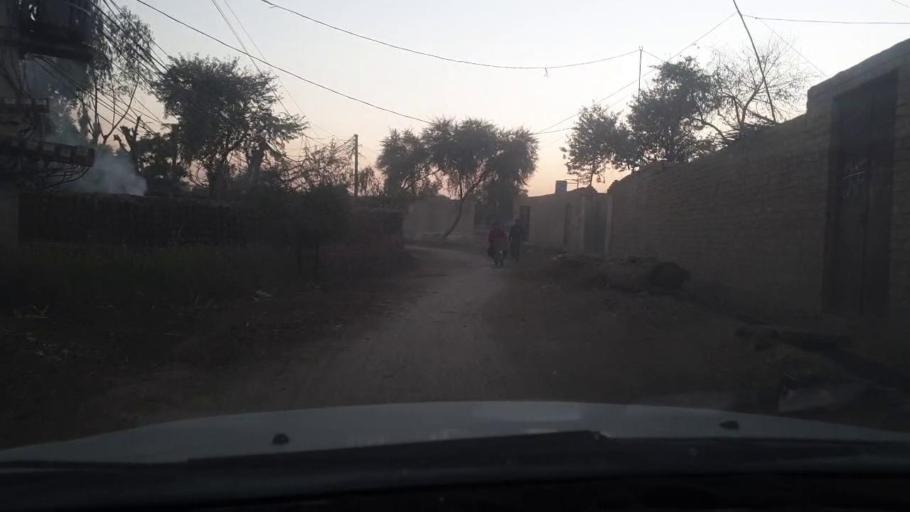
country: PK
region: Sindh
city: Ghotki
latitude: 28.0044
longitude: 69.3376
